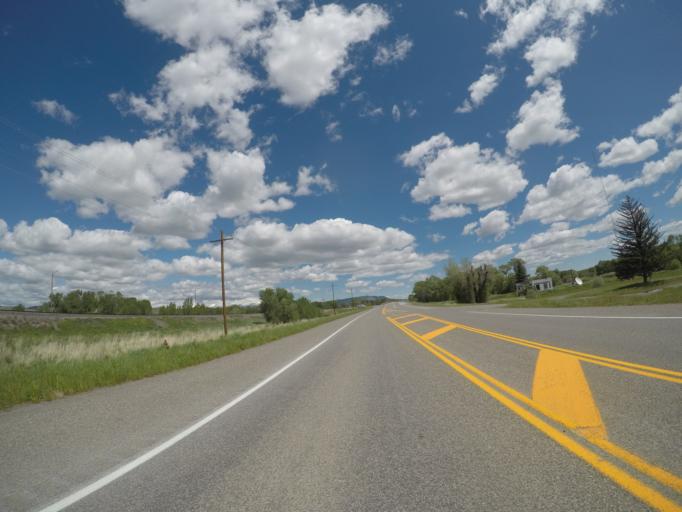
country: US
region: Montana
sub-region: Park County
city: Livingston
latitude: 45.6726
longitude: -110.5422
